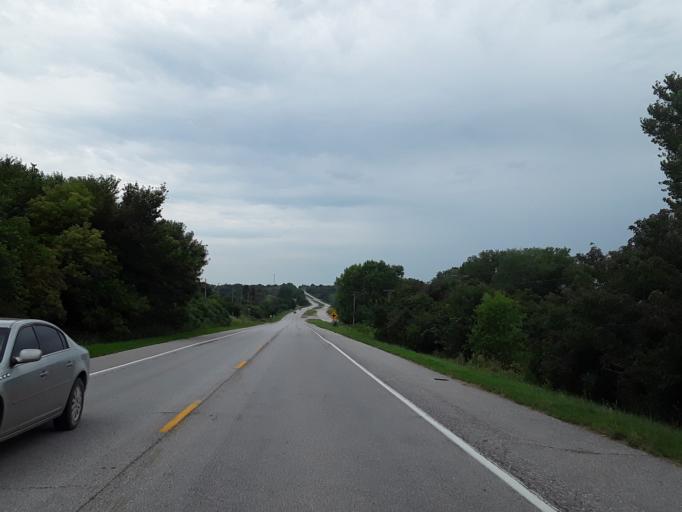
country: US
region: Nebraska
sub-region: Douglas County
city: Bennington
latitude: 41.3647
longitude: -96.0403
